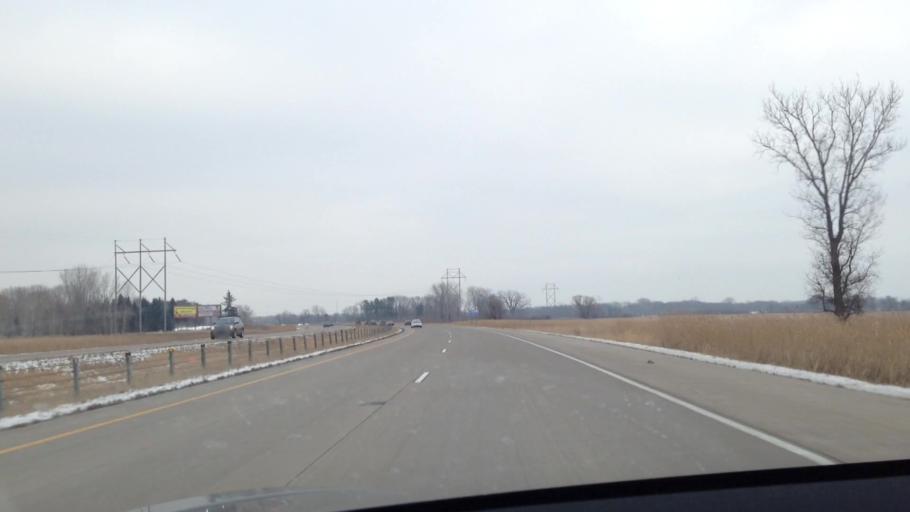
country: US
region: Minnesota
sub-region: Anoka County
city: Centerville
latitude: 45.1963
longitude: -93.0593
